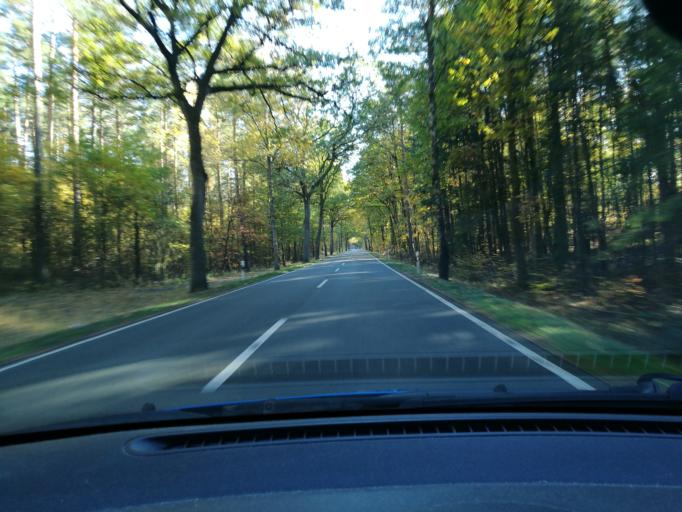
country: DE
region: Lower Saxony
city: Karwitz
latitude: 53.1206
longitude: 10.9863
